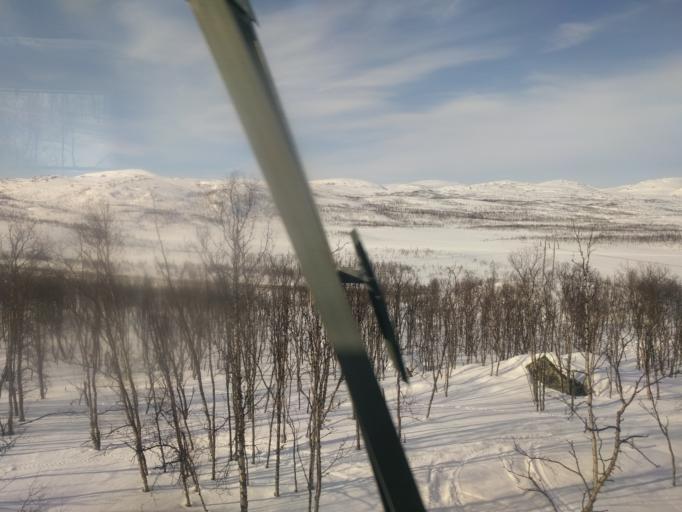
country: NO
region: Troms
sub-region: Bardu
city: Setermoen
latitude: 68.4278
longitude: 18.4728
